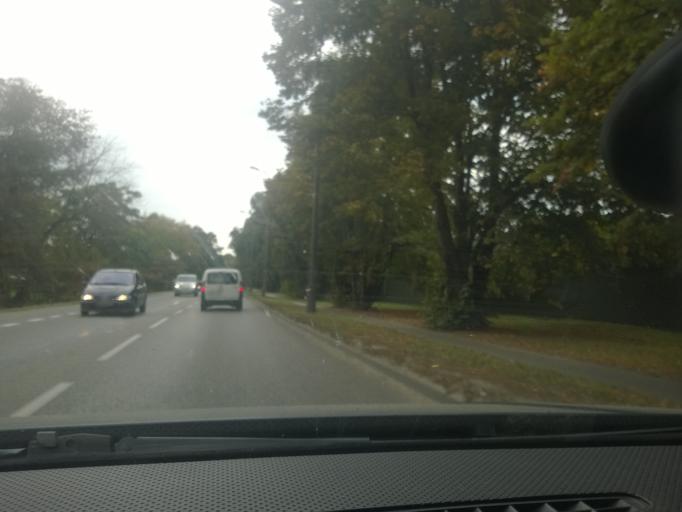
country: PL
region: Masovian Voivodeship
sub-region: Powiat pruszkowski
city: Pruszkow
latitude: 52.1734
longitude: 20.8014
